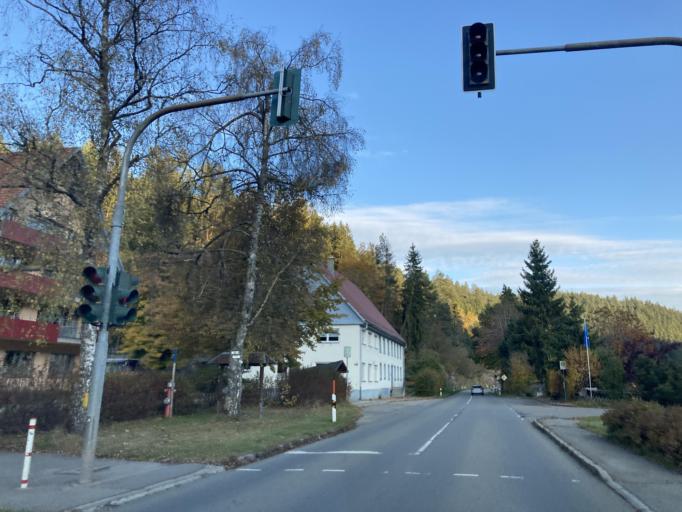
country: DE
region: Baden-Wuerttemberg
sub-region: Freiburg Region
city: Vohrenbach
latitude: 47.9950
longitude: 8.3442
